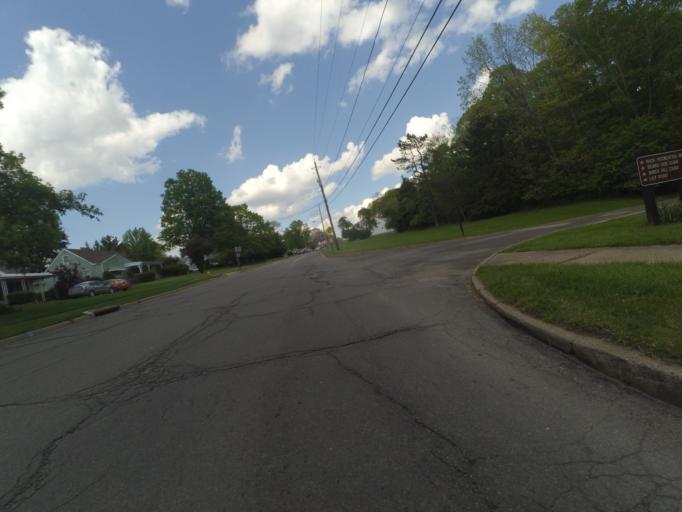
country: US
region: Ohio
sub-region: Mahoning County
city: Youngstown
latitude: 41.0871
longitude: -80.6985
